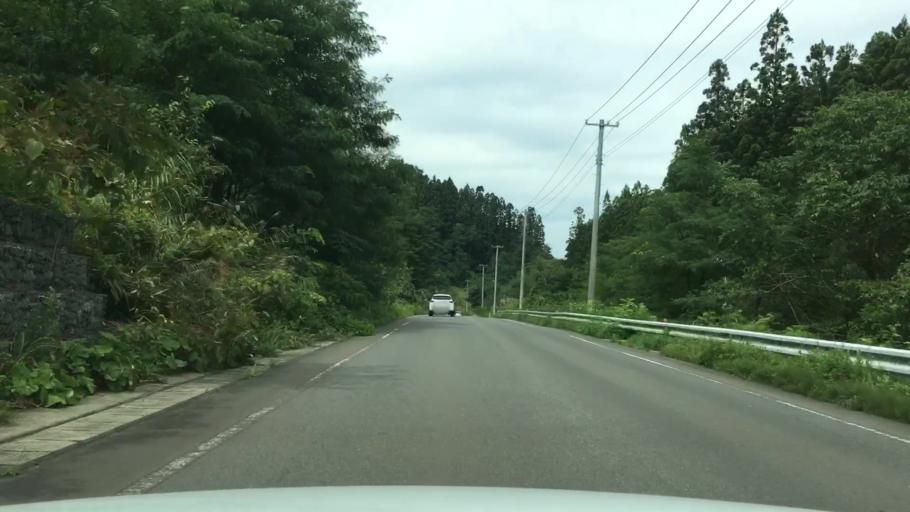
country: JP
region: Aomori
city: Shimokizukuri
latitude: 40.7425
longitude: 140.2436
